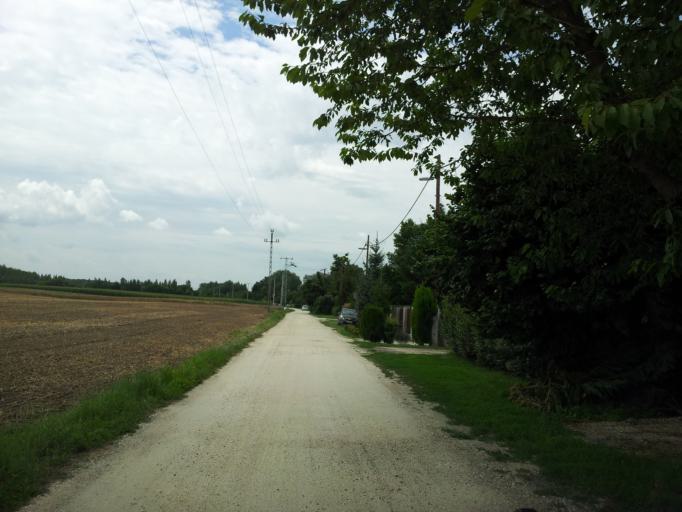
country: HU
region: Pest
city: Szigetcsep
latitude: 47.2341
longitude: 18.9756
